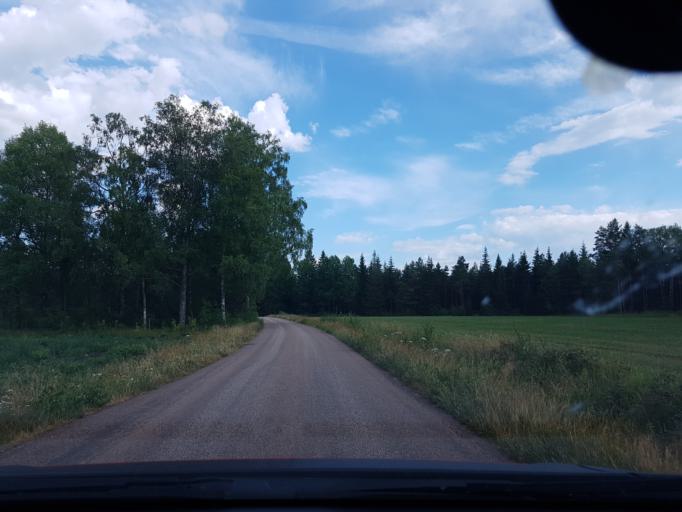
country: SE
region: Joenkoeping
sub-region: Gislaveds Kommun
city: Reftele
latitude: 57.2118
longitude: 13.5813
